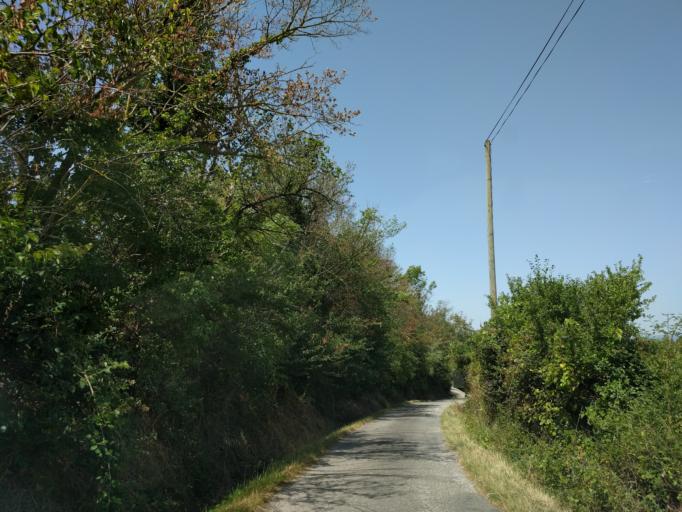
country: FR
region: Languedoc-Roussillon
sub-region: Departement de l'Aude
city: Cazilhac
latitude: 43.1979
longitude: 2.3786
